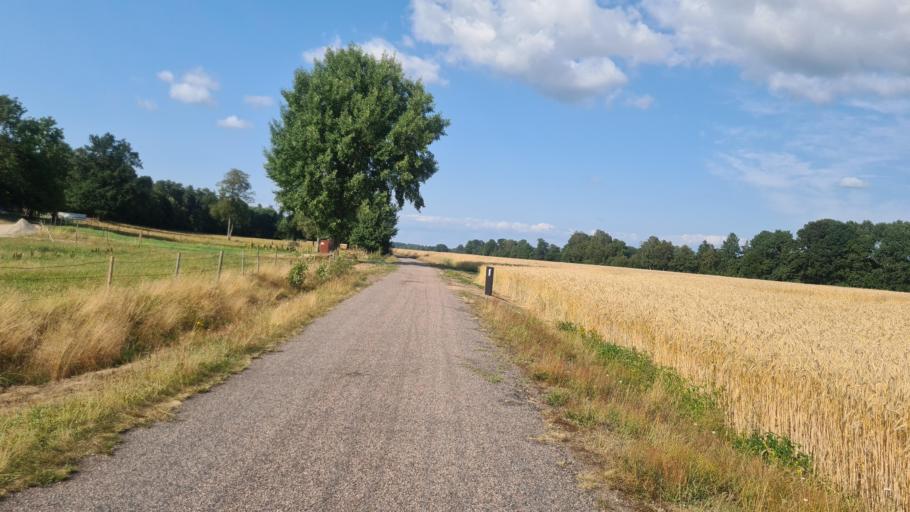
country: SE
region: Kronoberg
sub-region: Ljungby Kommun
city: Ljungby
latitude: 56.8006
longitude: 13.9135
